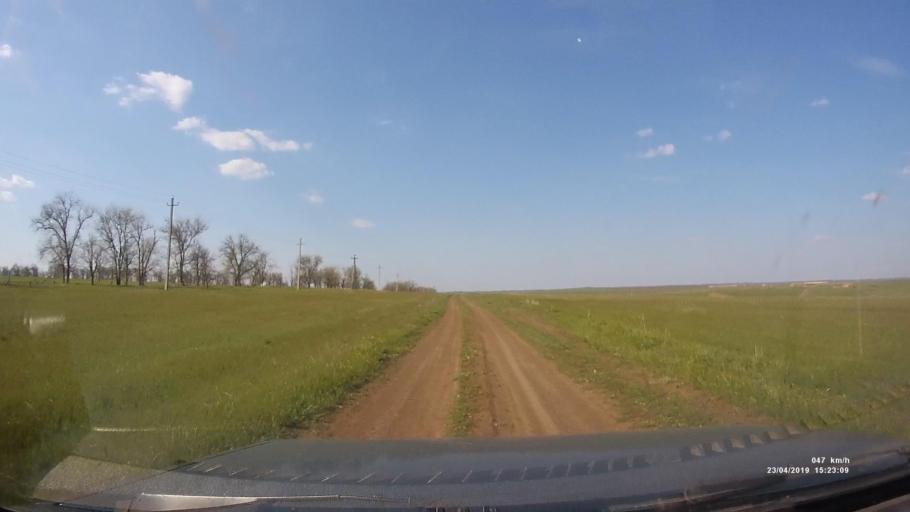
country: RU
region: Rostov
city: Remontnoye
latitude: 46.5336
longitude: 42.9698
